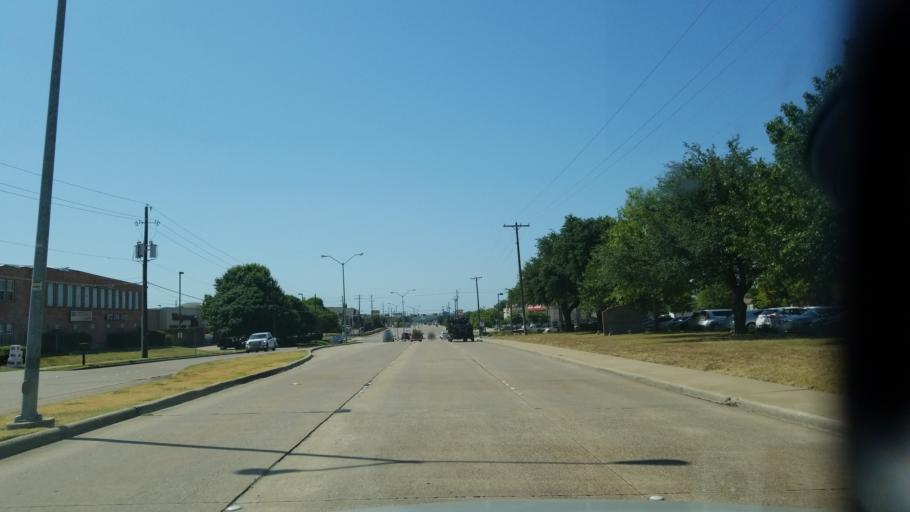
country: US
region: Texas
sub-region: Dallas County
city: Duncanville
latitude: 32.6493
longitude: -96.8914
